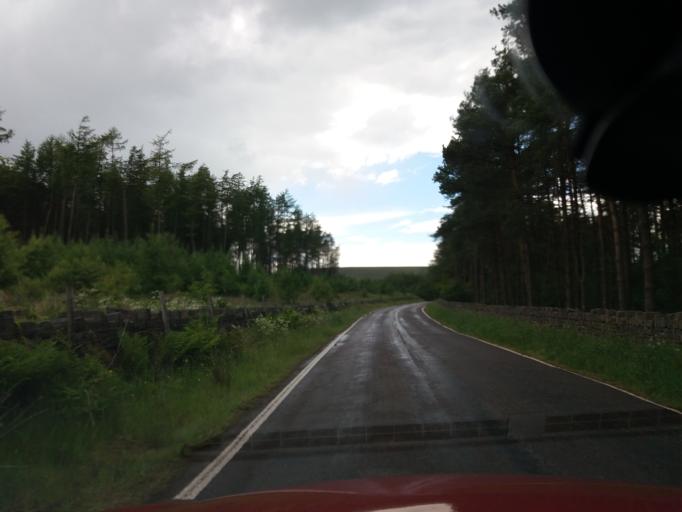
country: GB
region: England
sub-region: Blackburn with Darwen
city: Darwen
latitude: 53.6521
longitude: -2.4432
